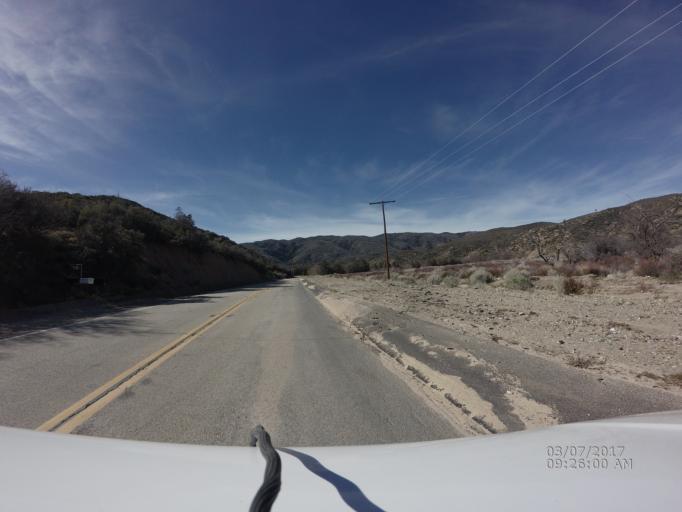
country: US
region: California
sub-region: Los Angeles County
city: Green Valley
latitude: 34.7444
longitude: -118.5987
